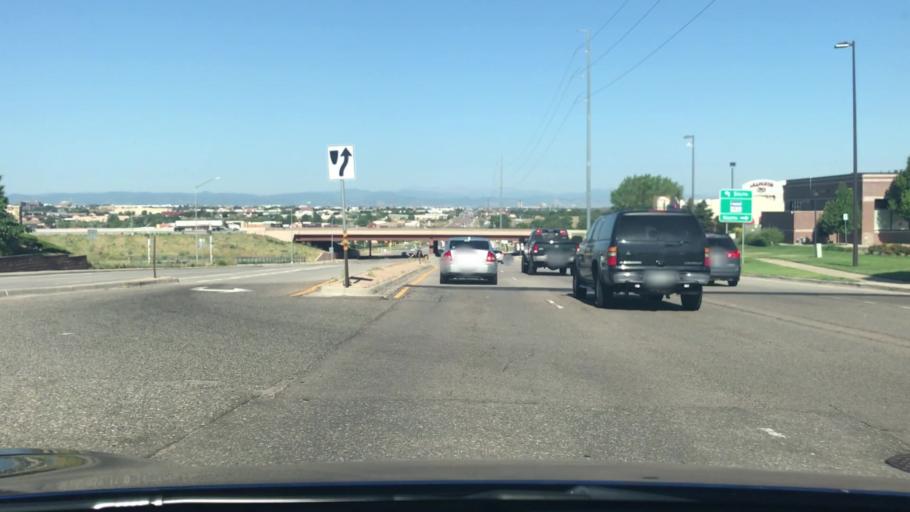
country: US
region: Colorado
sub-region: Arapahoe County
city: Dove Valley
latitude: 39.5950
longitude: -104.7989
